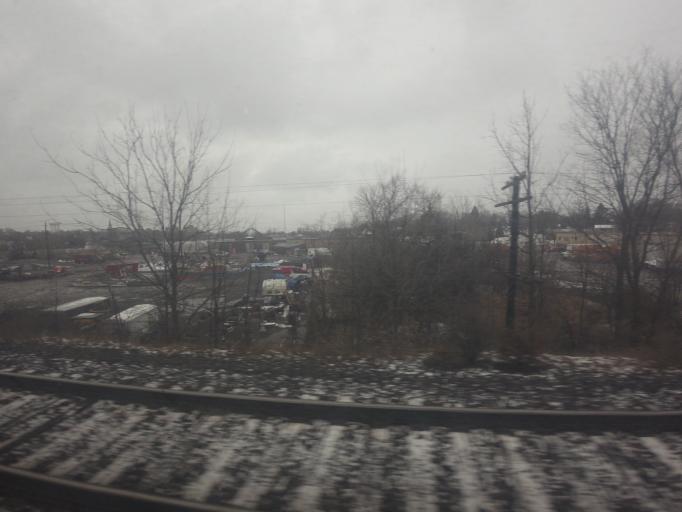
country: CA
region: Ontario
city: Belleville
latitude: 44.1720
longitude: -77.3961
